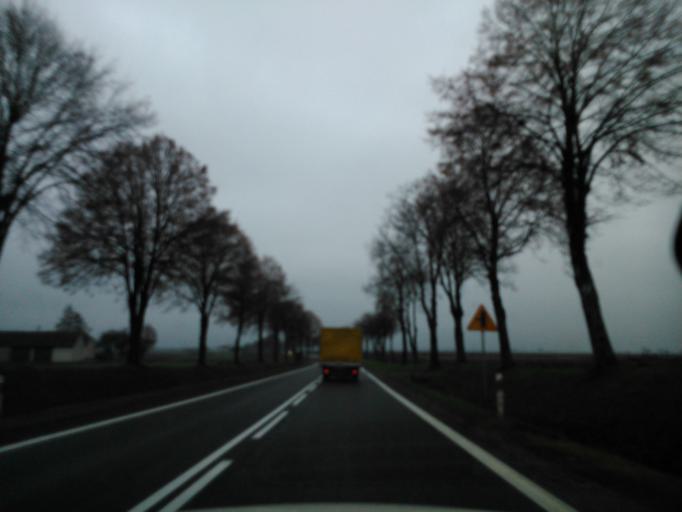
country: PL
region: Swietokrzyskie
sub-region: Powiat opatowski
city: Wojciechowice
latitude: 50.8314
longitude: 21.6175
